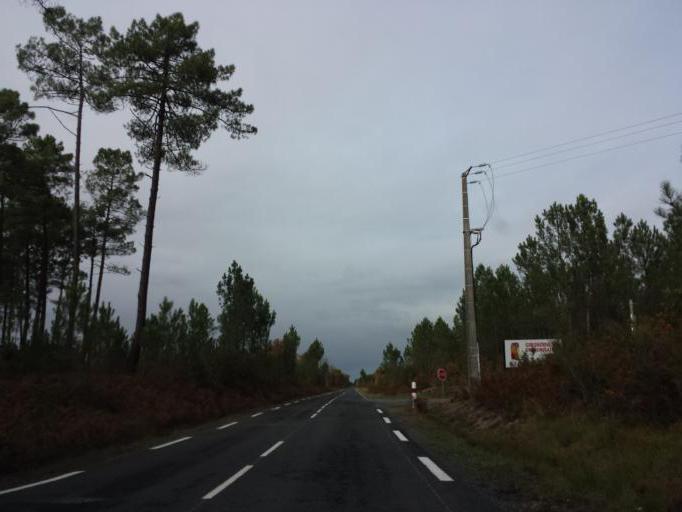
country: FR
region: Aquitaine
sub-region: Departement de la Gironde
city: Lacanau
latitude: 44.9490
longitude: -1.0661
